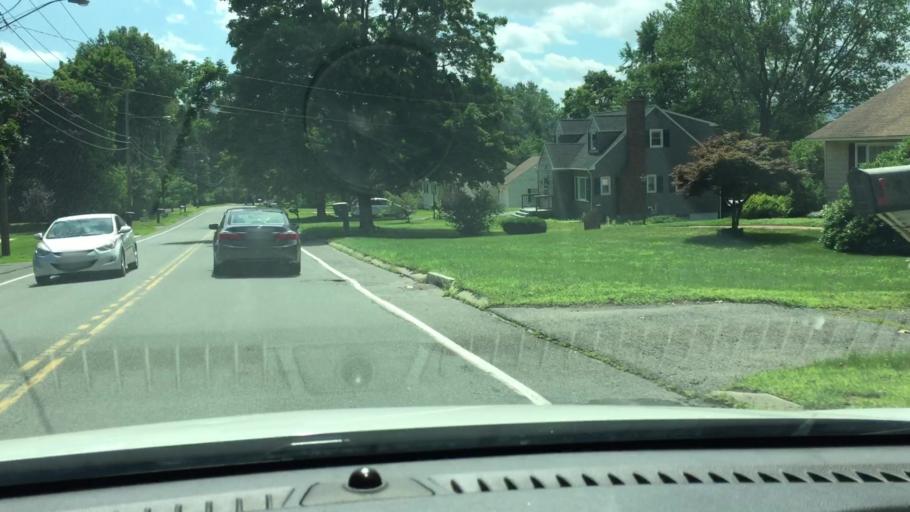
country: US
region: Massachusetts
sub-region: Berkshire County
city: Pittsfield
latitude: 42.4745
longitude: -73.2172
